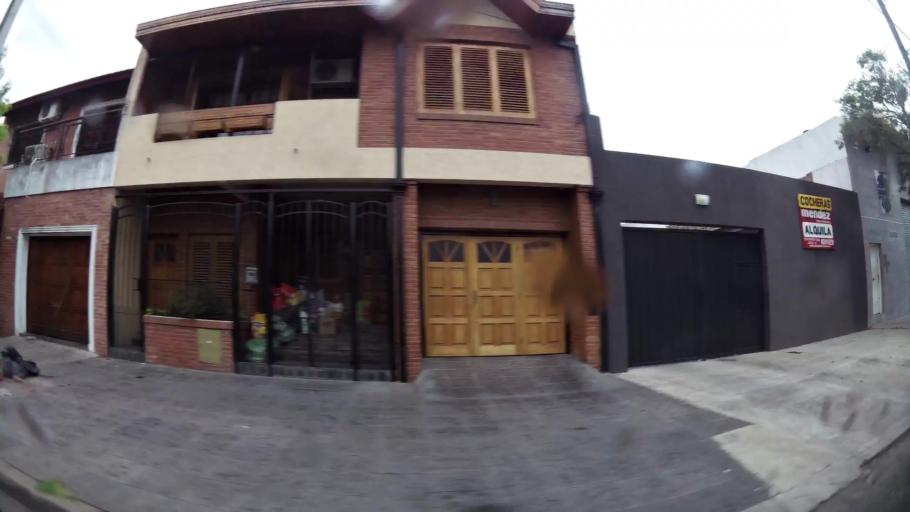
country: AR
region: Buenos Aires
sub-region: Partido de Lanus
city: Lanus
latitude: -34.6965
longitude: -58.4027
